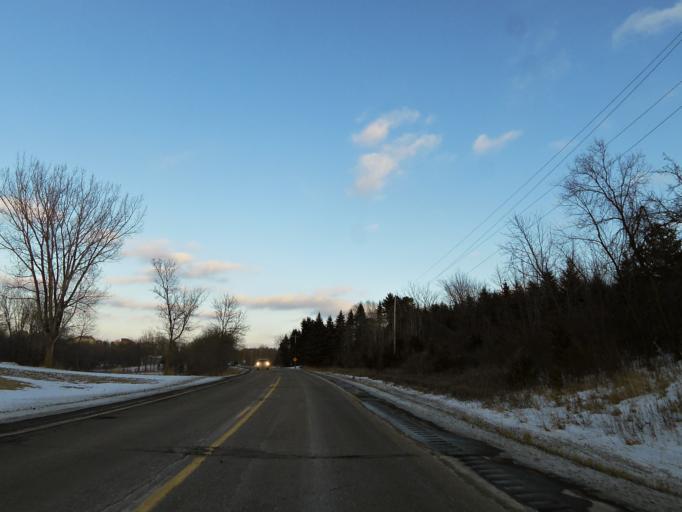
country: US
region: Minnesota
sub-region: Scott County
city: Elko New Market
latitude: 44.6374
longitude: -93.3437
